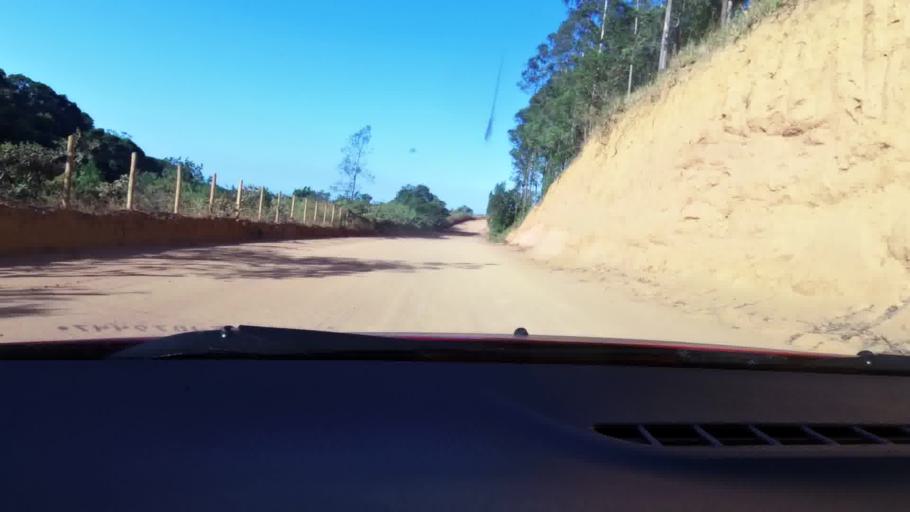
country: BR
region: Espirito Santo
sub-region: Guarapari
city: Guarapari
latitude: -20.5443
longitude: -40.4281
